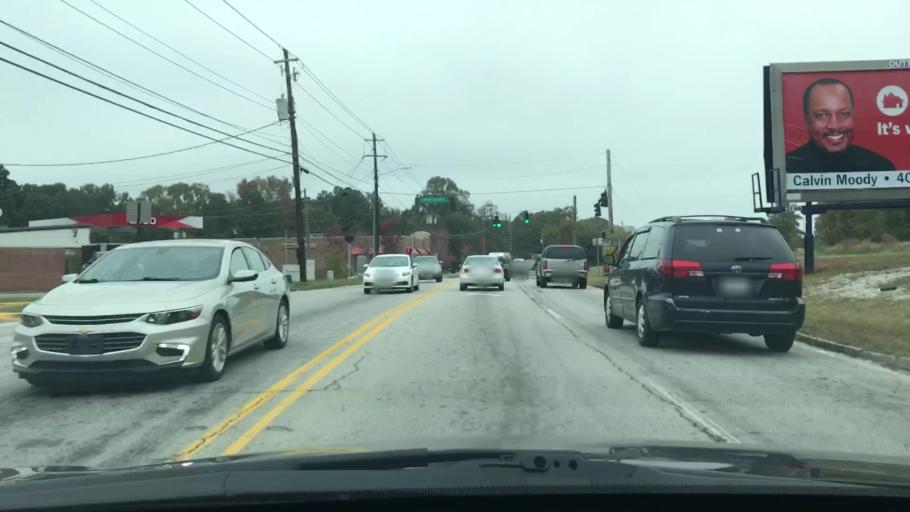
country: US
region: Georgia
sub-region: DeKalb County
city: Scottdale
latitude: 33.7945
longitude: -84.2634
